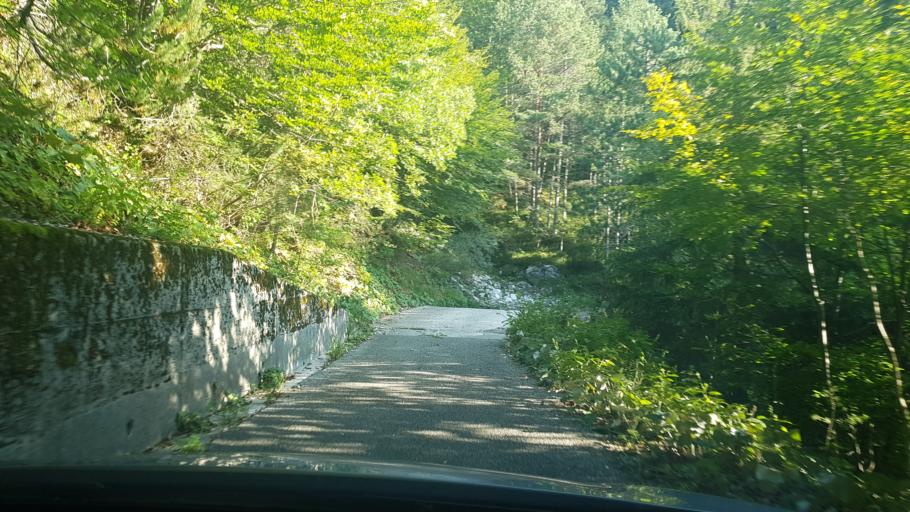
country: IT
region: Friuli Venezia Giulia
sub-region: Provincia di Udine
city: Moggio Udinese
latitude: 46.4465
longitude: 13.2151
